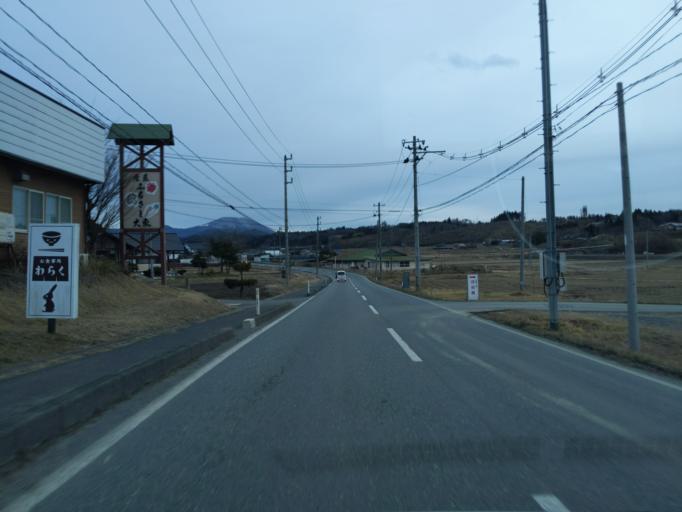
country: JP
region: Iwate
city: Ichinoseki
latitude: 39.0221
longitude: 141.3276
